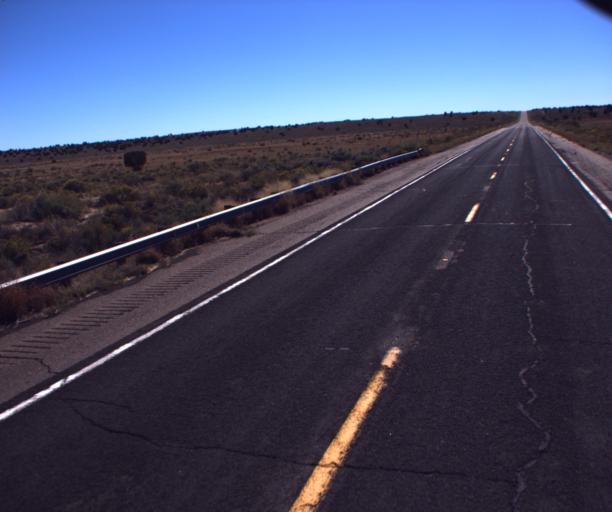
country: US
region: Arizona
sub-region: Navajo County
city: Snowflake
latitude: 34.6690
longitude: -109.7232
